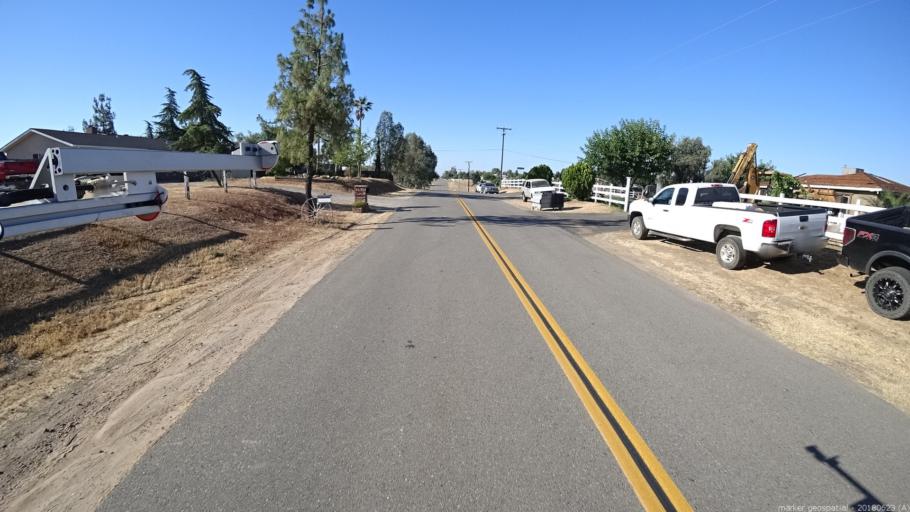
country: US
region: California
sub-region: Madera County
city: Bonadelle Ranchos-Madera Ranchos
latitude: 36.9650
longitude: -119.8015
